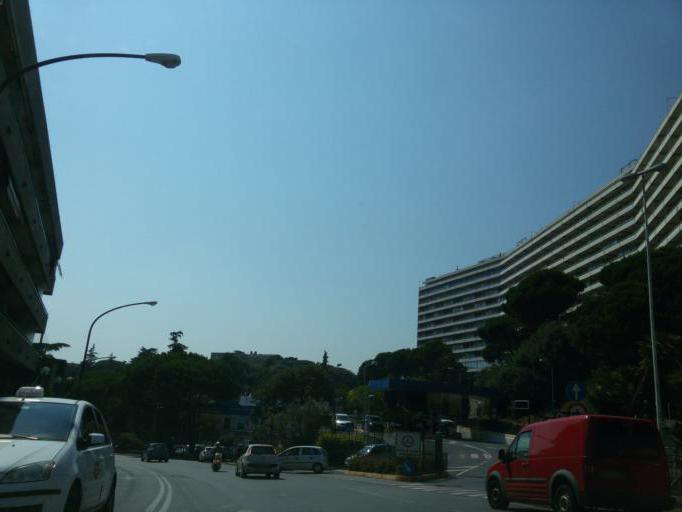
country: IT
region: Liguria
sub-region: Provincia di Genova
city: Genoa
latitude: 44.4084
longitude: 8.9769
